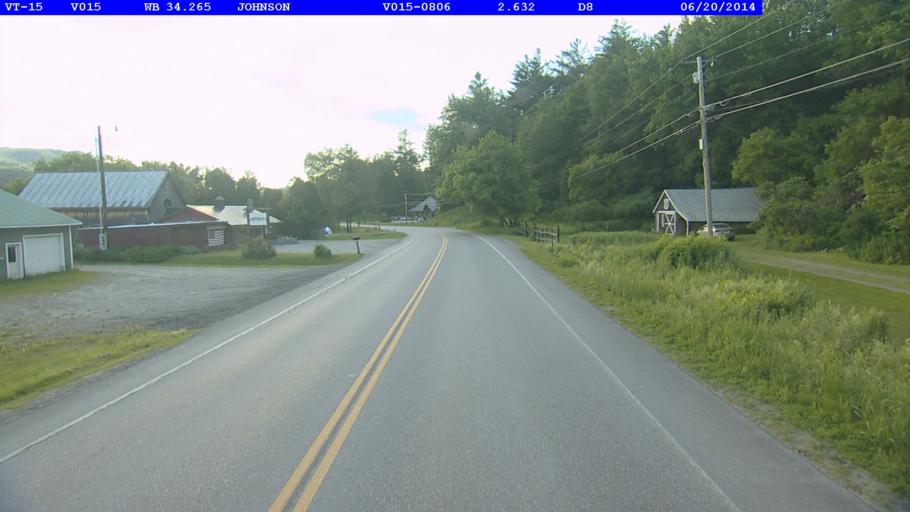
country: US
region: Vermont
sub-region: Lamoille County
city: Johnson
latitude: 44.6425
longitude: -72.7045
